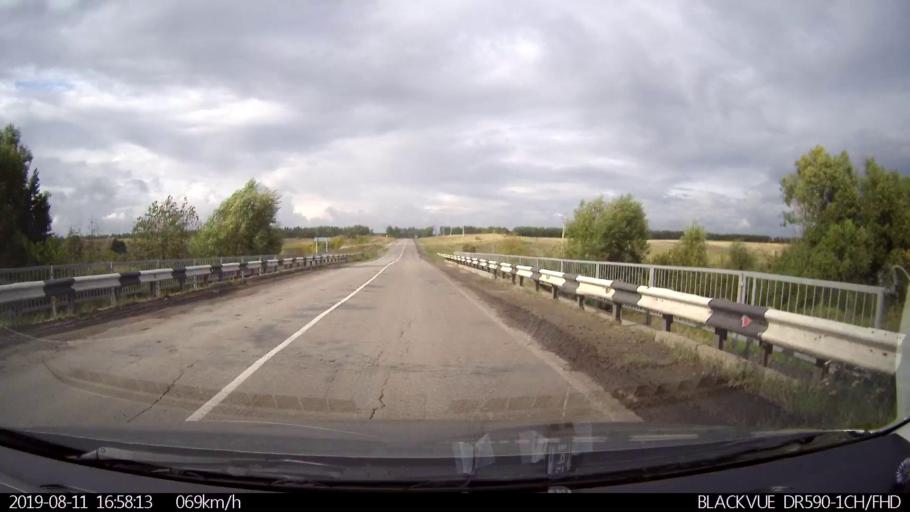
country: RU
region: Ulyanovsk
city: Mayna
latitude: 54.3062
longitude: 47.6555
